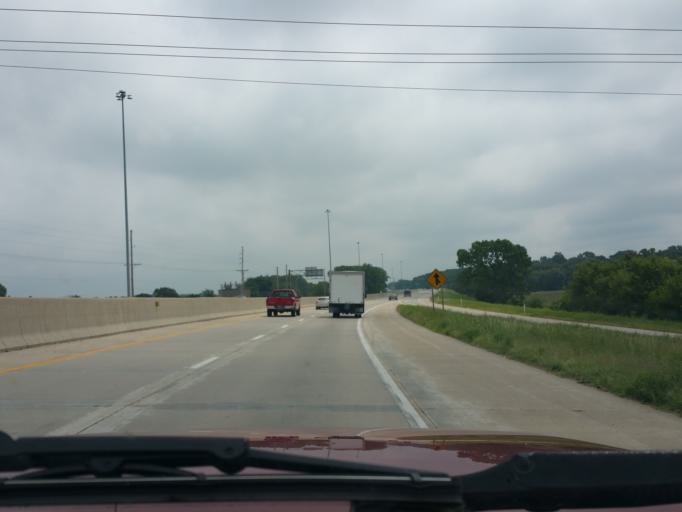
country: US
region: Kansas
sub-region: Shawnee County
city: Topeka
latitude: 39.0702
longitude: -95.7045
